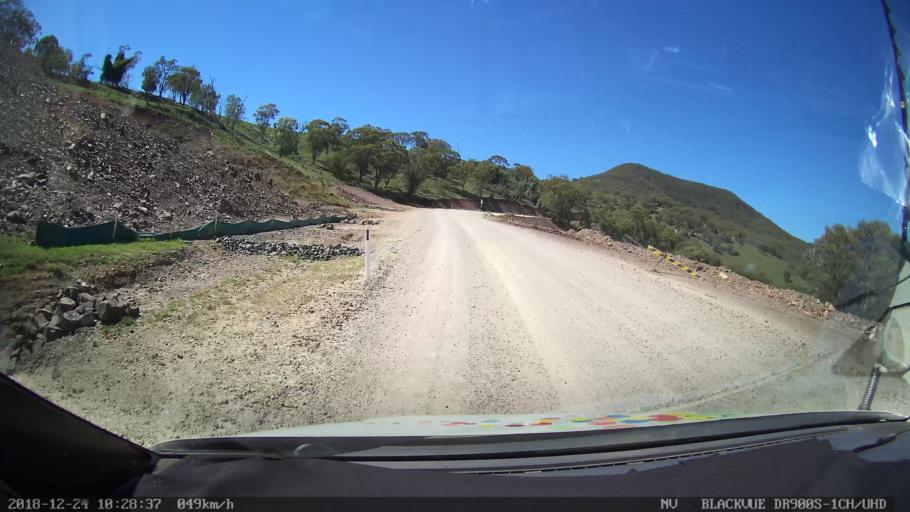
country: AU
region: New South Wales
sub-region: Liverpool Plains
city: Quirindi
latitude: -31.8270
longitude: 150.5315
